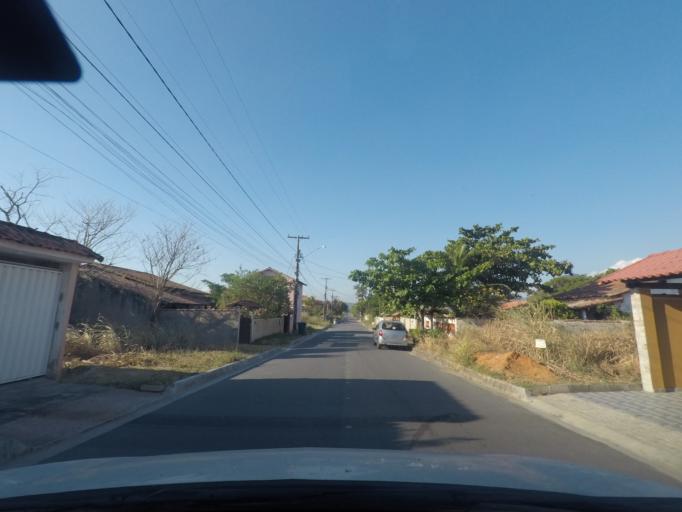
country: BR
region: Rio de Janeiro
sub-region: Marica
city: Marica
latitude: -22.9662
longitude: -42.9388
